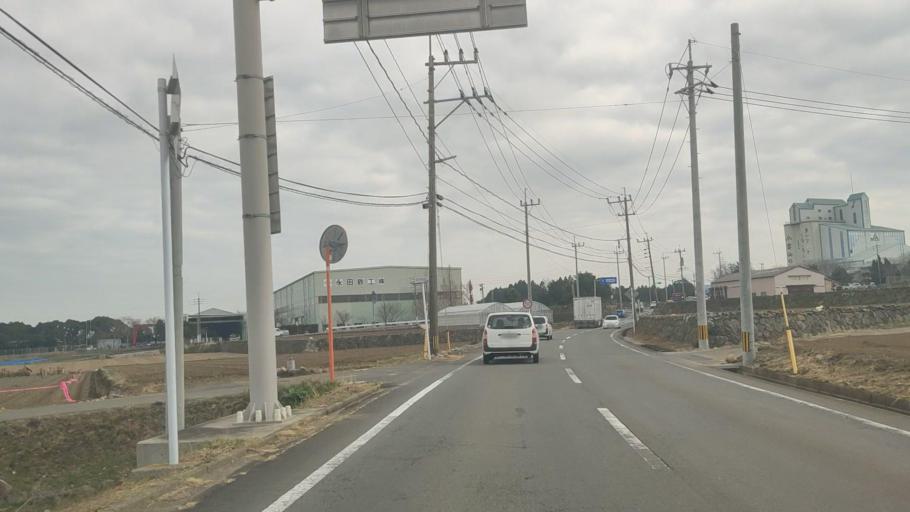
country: JP
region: Nagasaki
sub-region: Isahaya-shi
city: Isahaya
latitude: 32.8188
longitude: 130.1787
